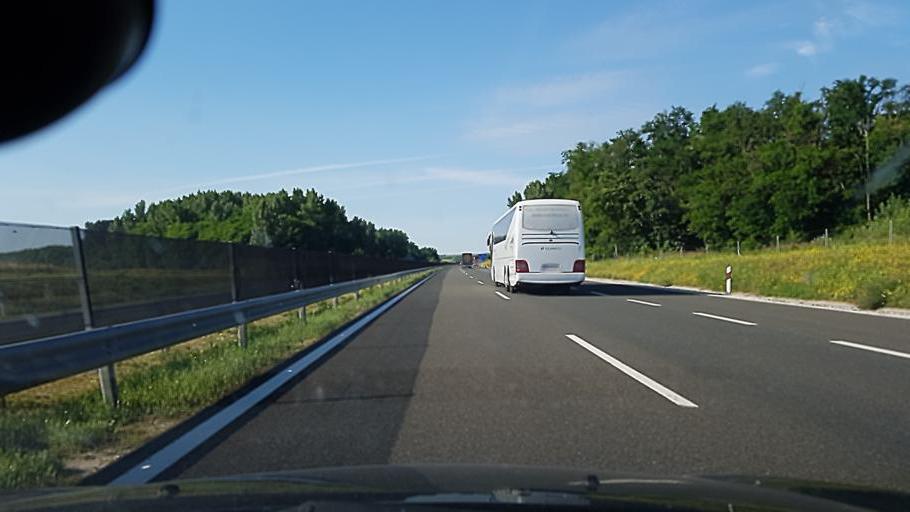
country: HU
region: Fejer
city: Baracs
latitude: 46.8521
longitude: 18.8745
